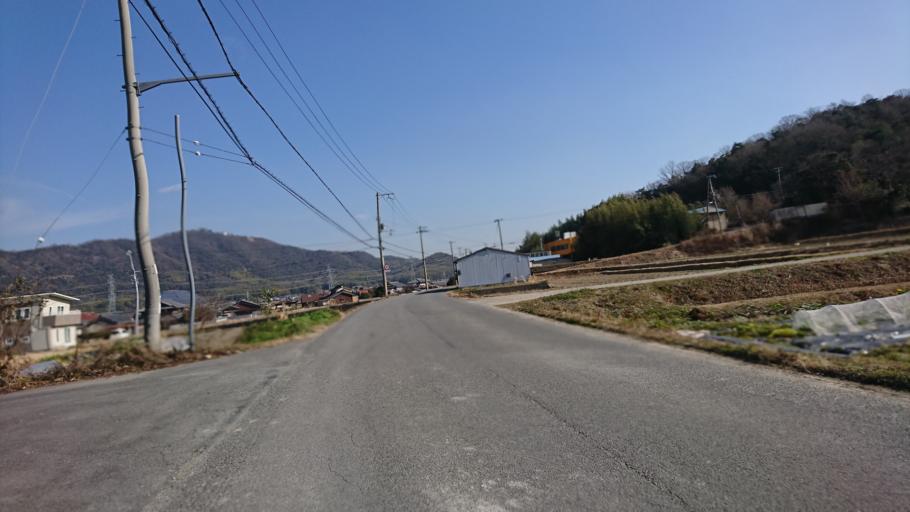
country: JP
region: Hyogo
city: Kakogawacho-honmachi
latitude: 34.8237
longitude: 134.8360
